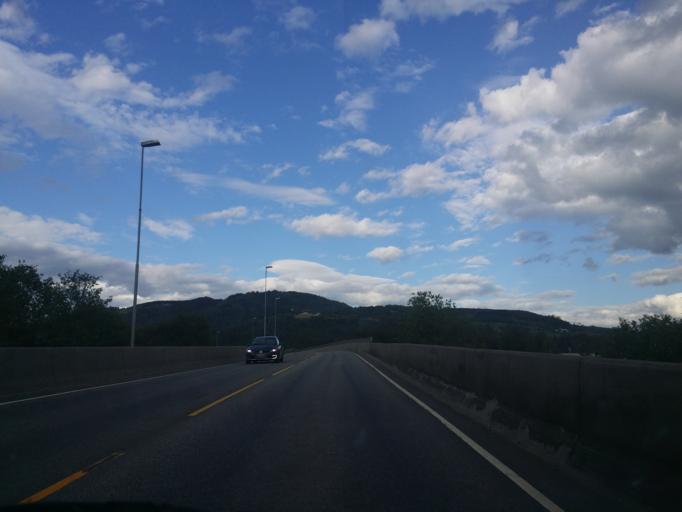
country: NO
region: Hedmark
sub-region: Ringsaker
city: Brumunddal
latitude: 60.8809
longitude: 10.9331
